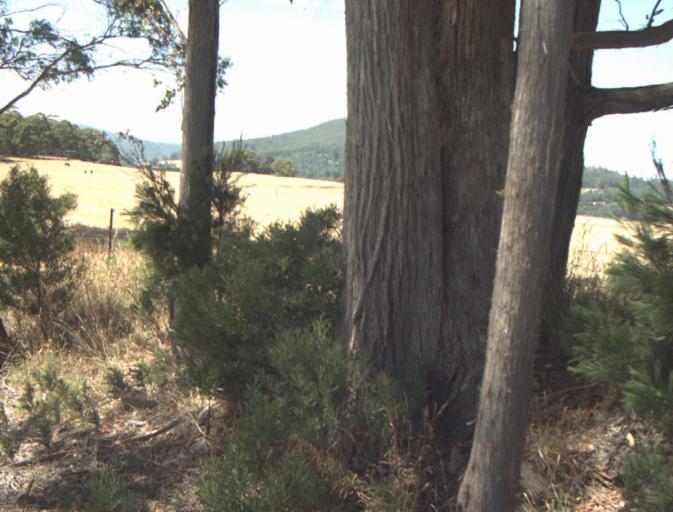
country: AU
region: Tasmania
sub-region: Launceston
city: Mayfield
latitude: -41.2477
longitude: 147.1679
